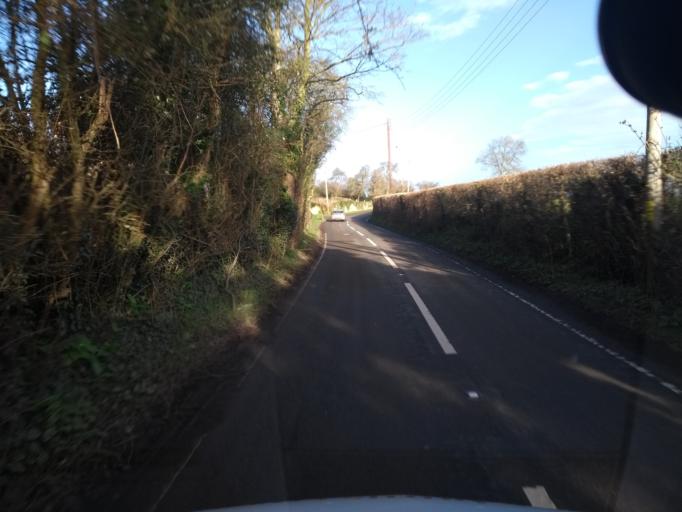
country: GB
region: England
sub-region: Somerset
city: Wedmore
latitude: 51.2144
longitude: -2.7820
